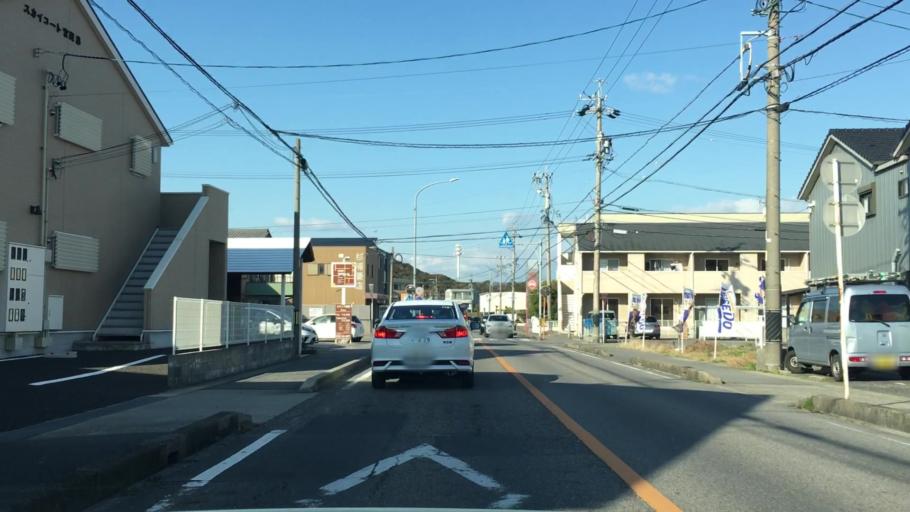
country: JP
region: Aichi
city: Nishio
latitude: 34.8665
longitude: 137.0729
